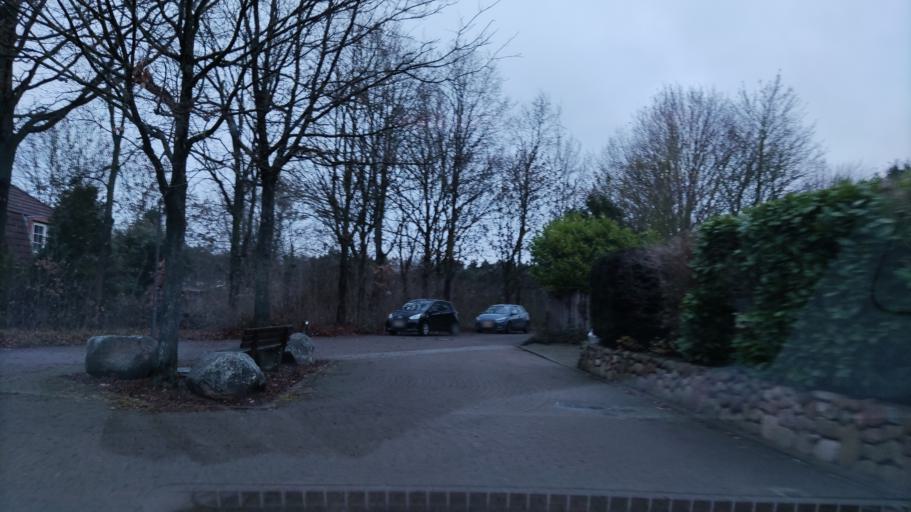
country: DE
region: Lower Saxony
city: Vogelsen
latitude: 53.2766
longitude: 10.3580
